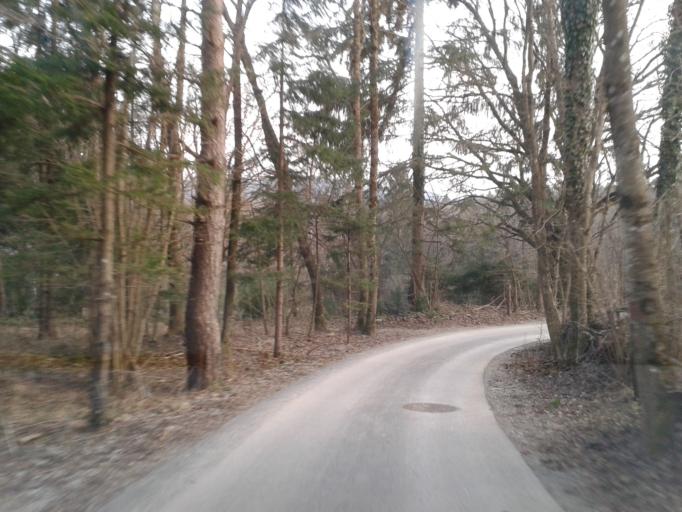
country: AT
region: Styria
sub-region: Politischer Bezirk Graz-Umgebung
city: Sankt Radegund bei Graz
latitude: 47.1527
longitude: 15.4503
